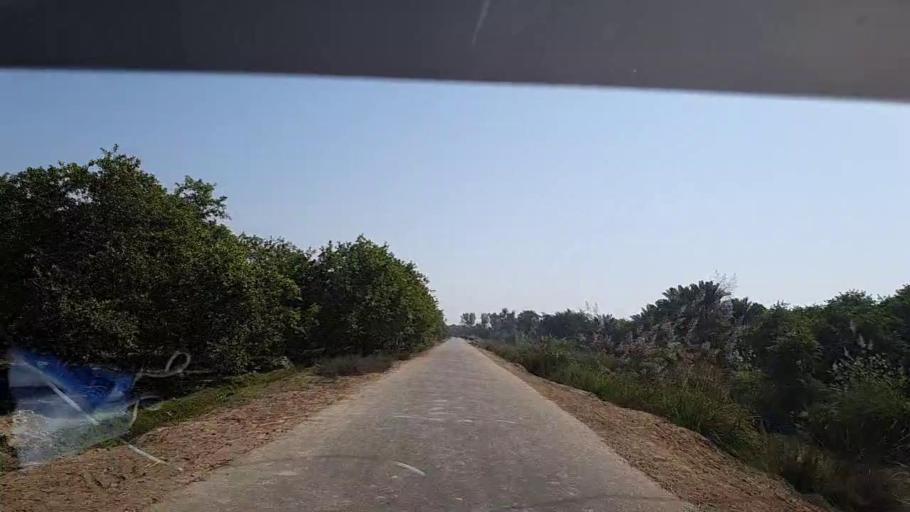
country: PK
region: Sindh
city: Larkana
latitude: 27.6031
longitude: 68.2646
